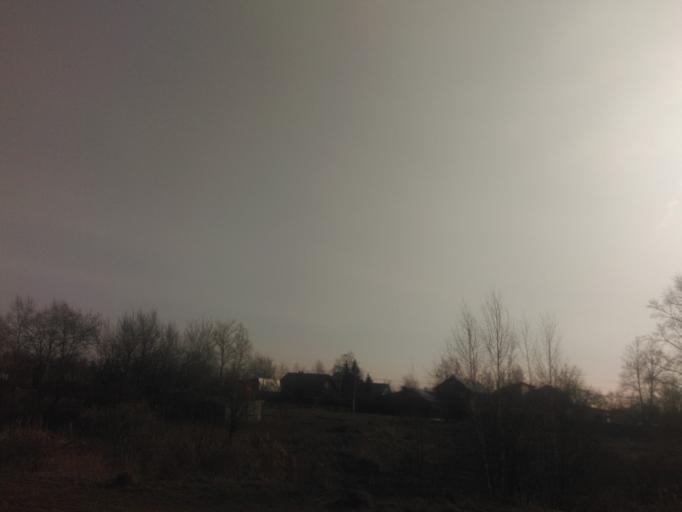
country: RU
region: Moskovskaya
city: Kokoshkino
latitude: 55.5904
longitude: 37.1176
